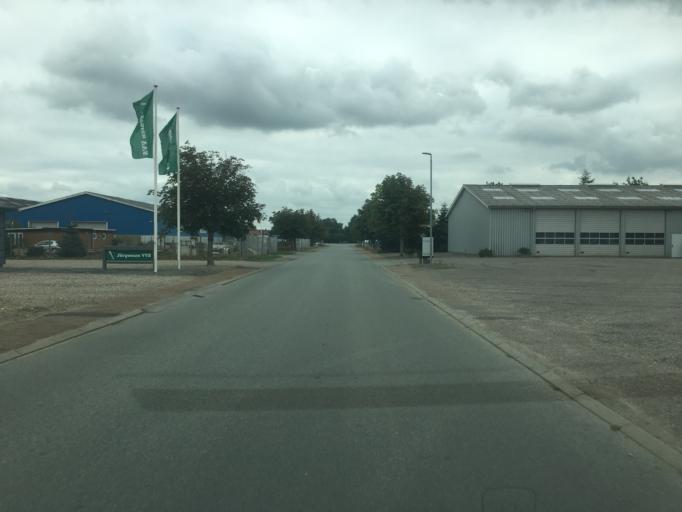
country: DK
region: South Denmark
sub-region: Tonder Kommune
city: Tonder
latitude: 54.9492
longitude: 8.8646
